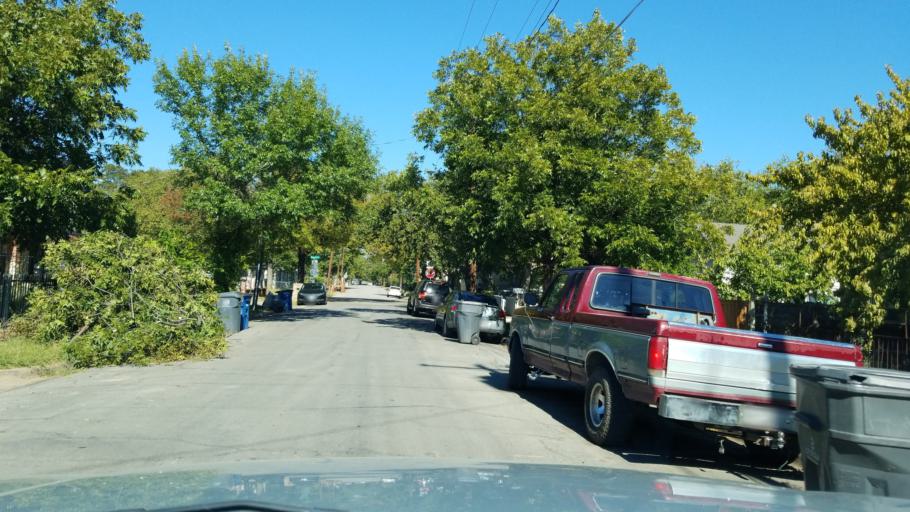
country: US
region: Texas
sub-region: Dallas County
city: Highland Park
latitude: 32.7969
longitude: -96.7537
